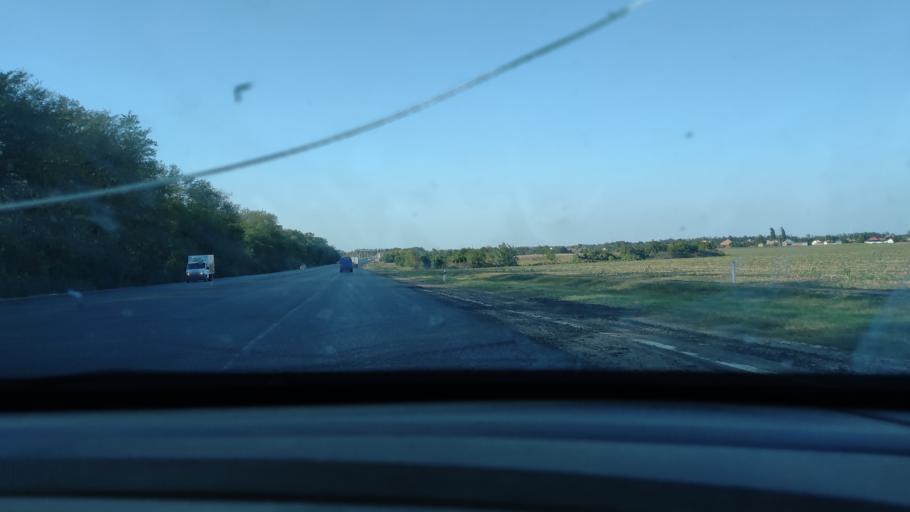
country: RU
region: Krasnodarskiy
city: Medvedovskaya
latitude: 45.5079
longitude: 38.9415
